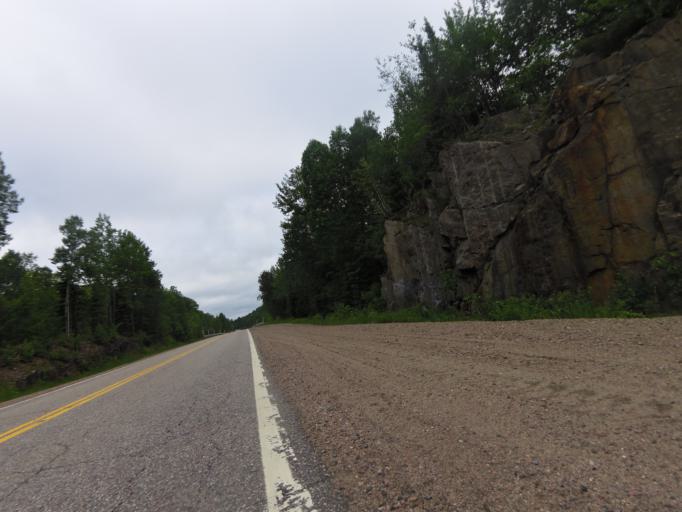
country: CA
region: Quebec
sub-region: Outaouais
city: Shawville
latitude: 45.9132
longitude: -76.3236
